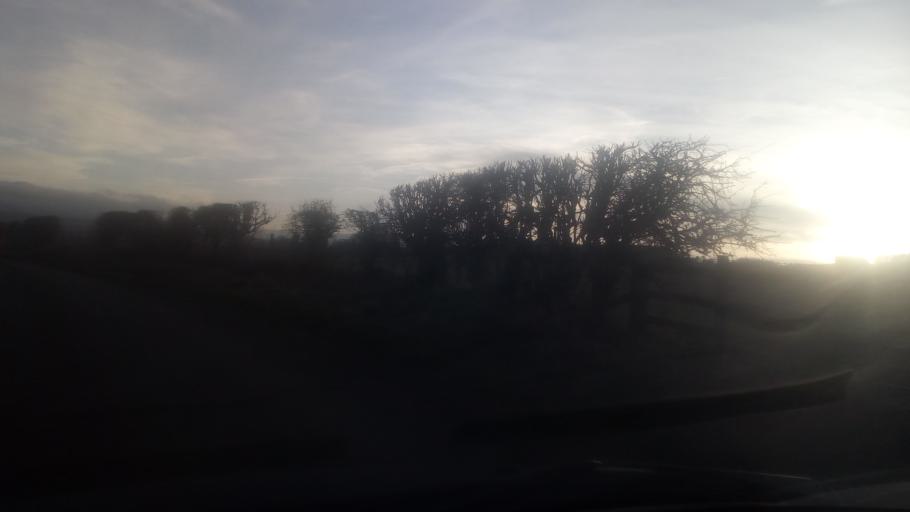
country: GB
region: Scotland
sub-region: The Scottish Borders
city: Jedburgh
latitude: 55.4900
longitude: -2.5532
